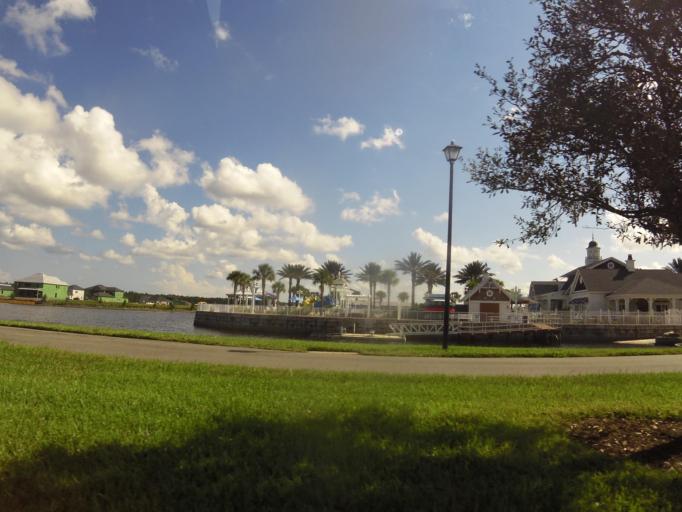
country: US
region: Florida
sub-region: Saint Johns County
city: Palm Valley
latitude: 30.0748
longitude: -81.4695
